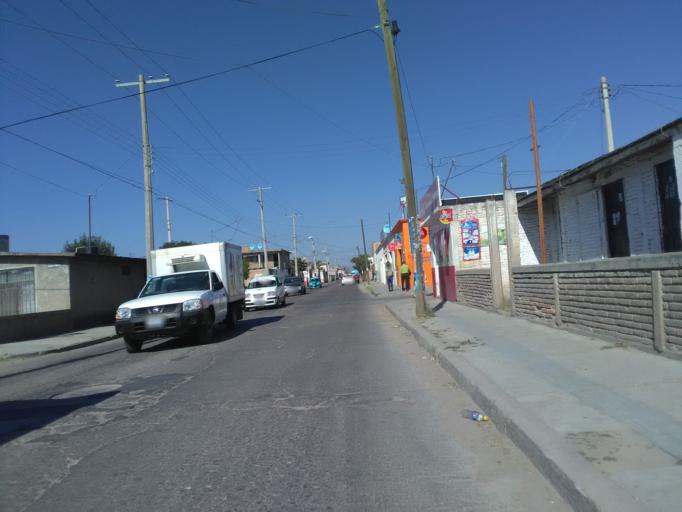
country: MX
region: Durango
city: Victoria de Durango
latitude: 24.0133
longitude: -104.6393
